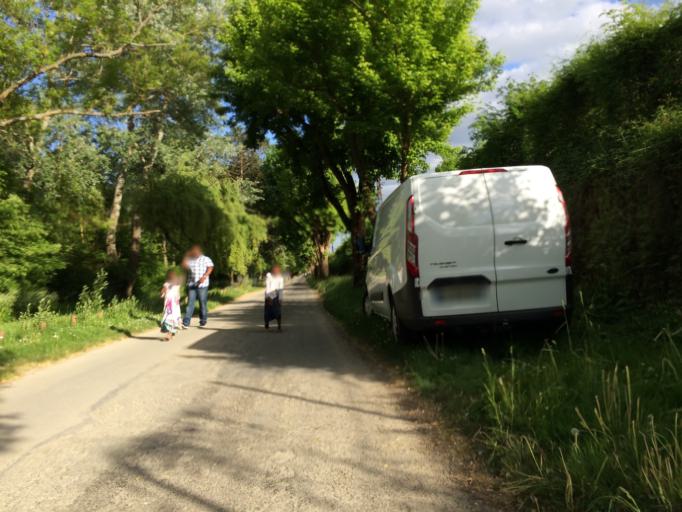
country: FR
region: Ile-de-France
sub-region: Departement de l'Essonne
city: Ris-Orangis
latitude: 48.6530
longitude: 2.4286
